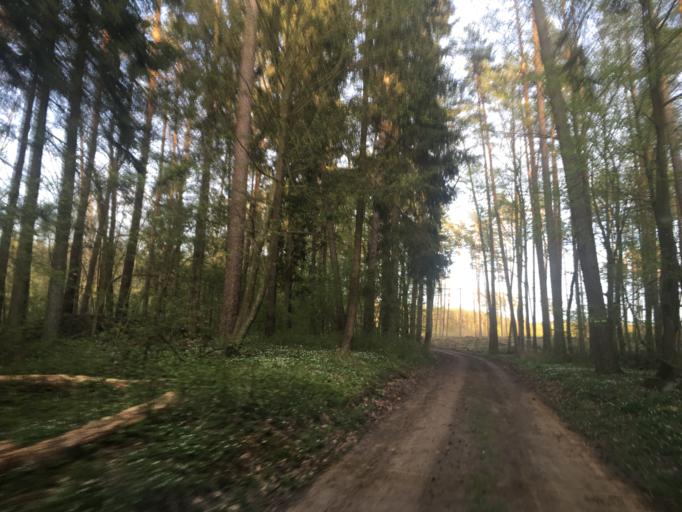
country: PL
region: Kujawsko-Pomorskie
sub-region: Powiat brodnicki
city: Gorzno
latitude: 53.2033
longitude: 19.6810
